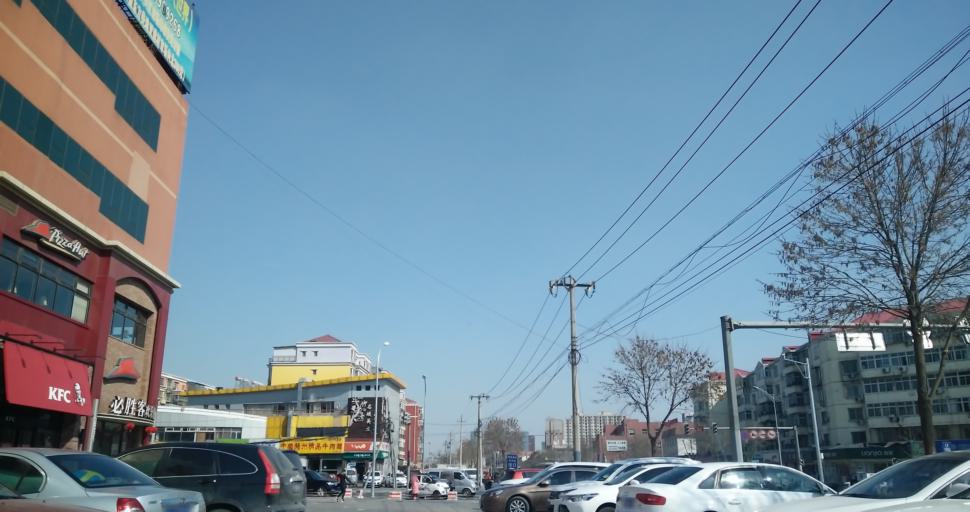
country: CN
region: Beijing
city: Jiugong
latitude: 39.8038
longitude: 116.4372
